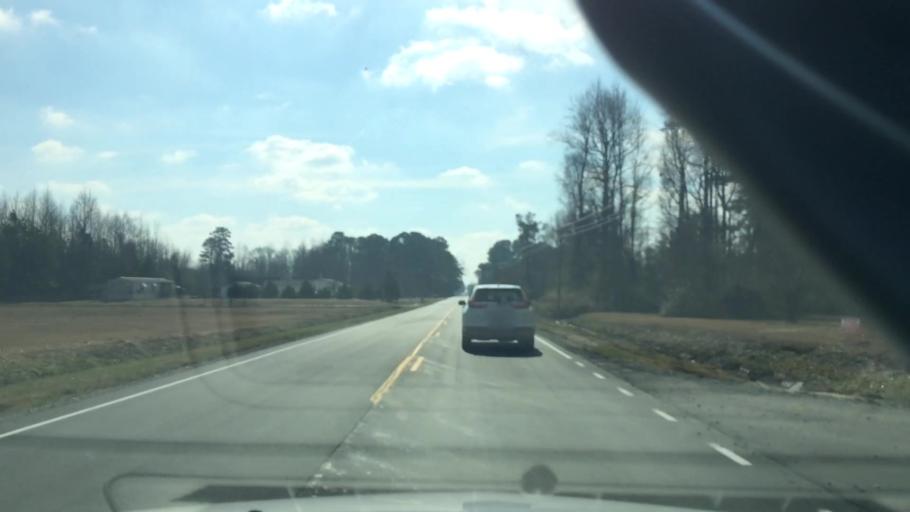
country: US
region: North Carolina
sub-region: Duplin County
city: Beulaville
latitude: 34.9672
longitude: -77.7631
